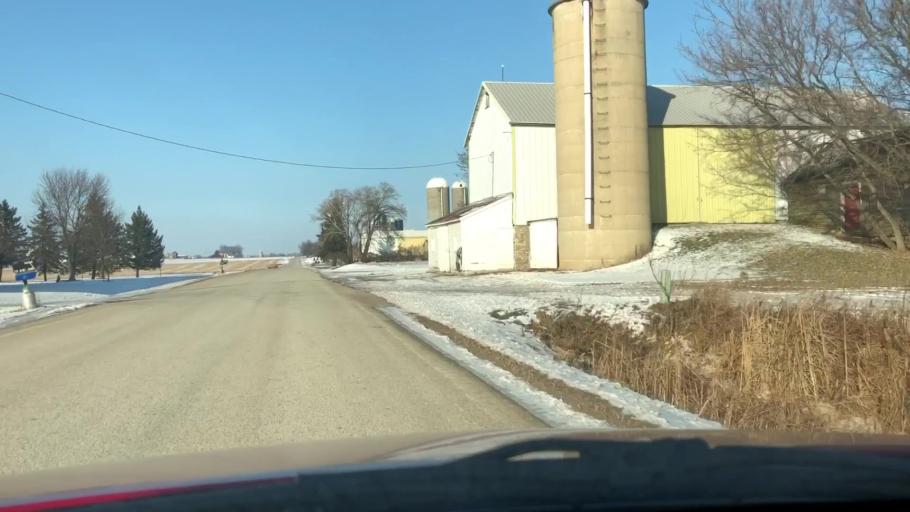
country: US
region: Wisconsin
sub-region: Outagamie County
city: Seymour
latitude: 44.4899
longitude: -88.3090
